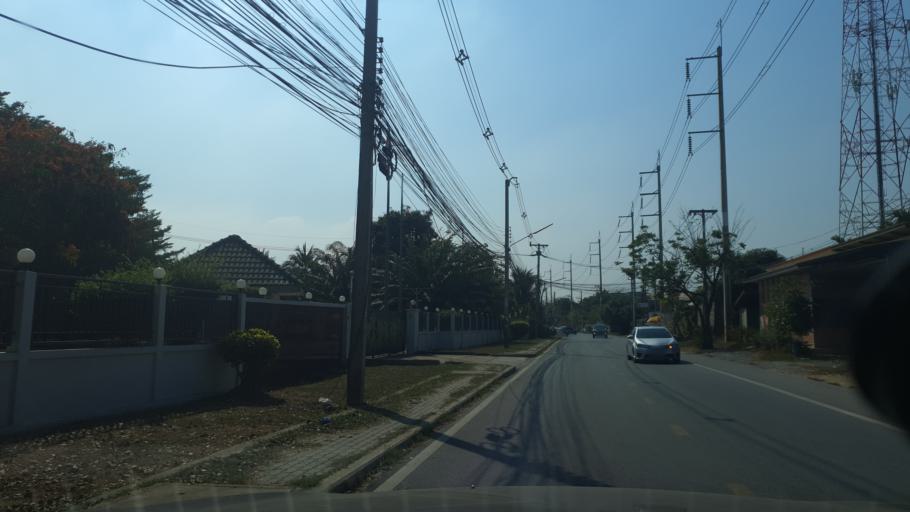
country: TH
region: Nakhon Pathom
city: Salaya
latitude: 13.7828
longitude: 100.2694
